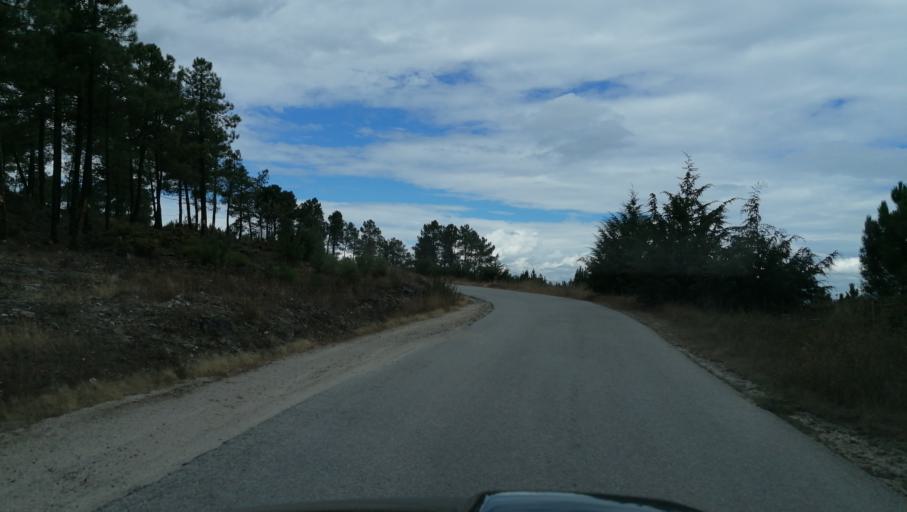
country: PT
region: Vila Real
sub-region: Vila Pouca de Aguiar
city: Vila Pouca de Aguiar
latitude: 41.5556
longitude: -7.6294
